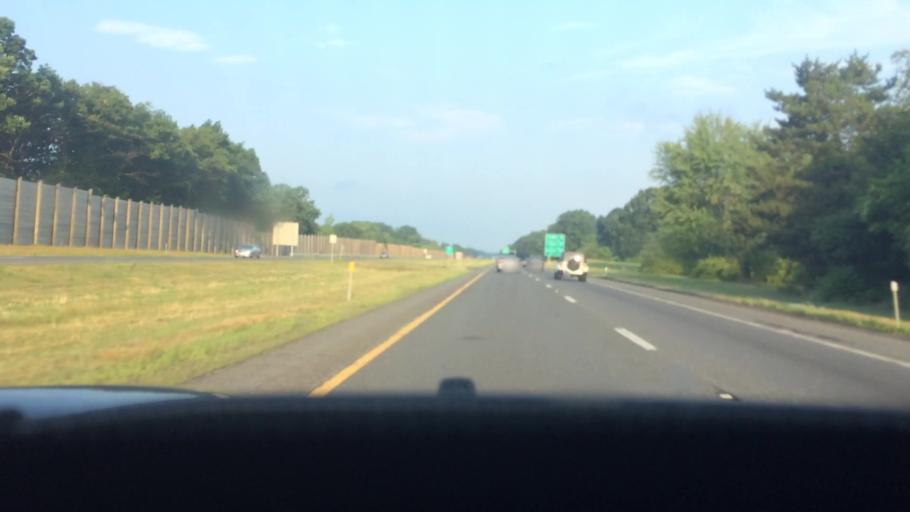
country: US
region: Massachusetts
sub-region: Hampden County
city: Ludlow
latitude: 42.1660
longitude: -72.4935
